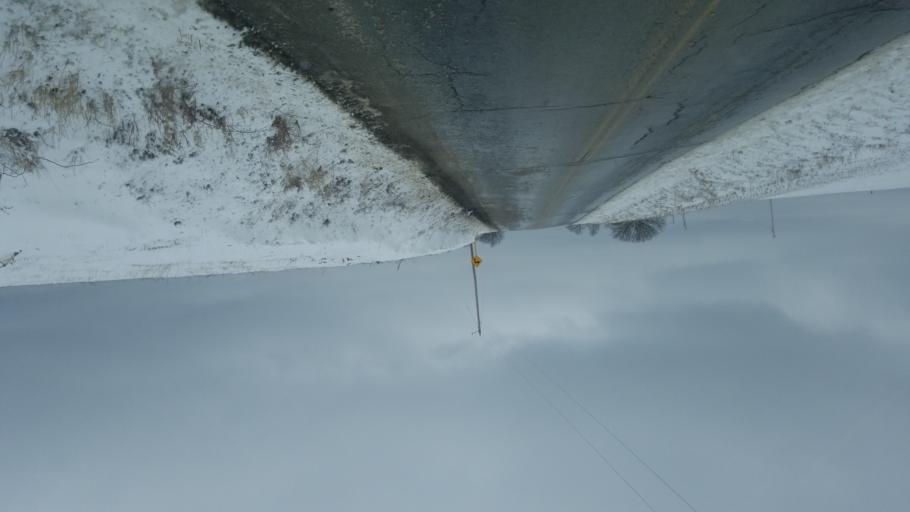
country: US
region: Ohio
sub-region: Knox County
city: Oak Hill
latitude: 40.4900
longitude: -82.1281
